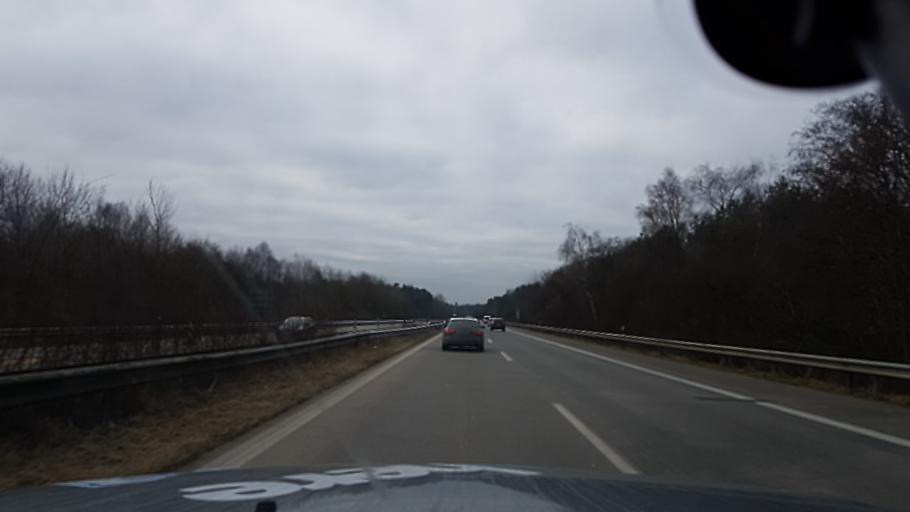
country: DE
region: Schleswig-Holstein
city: Ratekau
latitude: 53.9381
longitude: 10.7403
